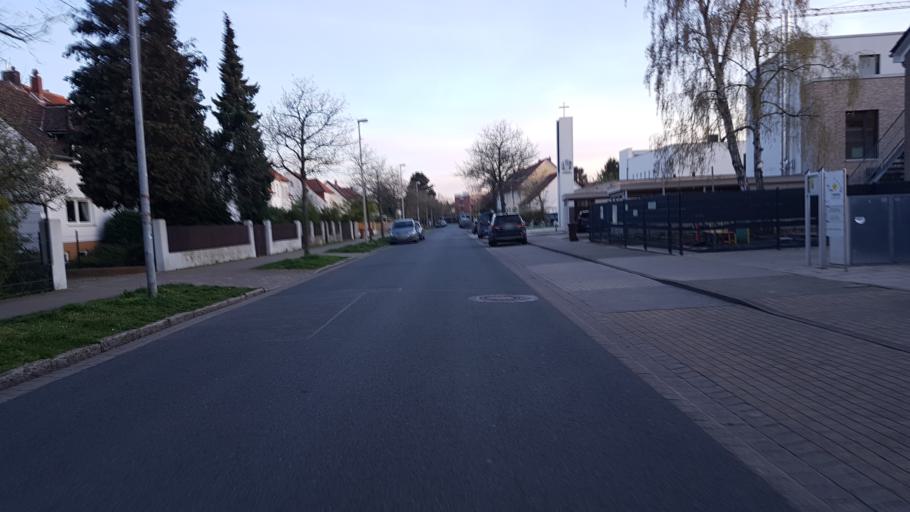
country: DE
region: Lower Saxony
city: Isernhagen Farster Bauerschaft
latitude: 52.4223
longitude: 9.8059
